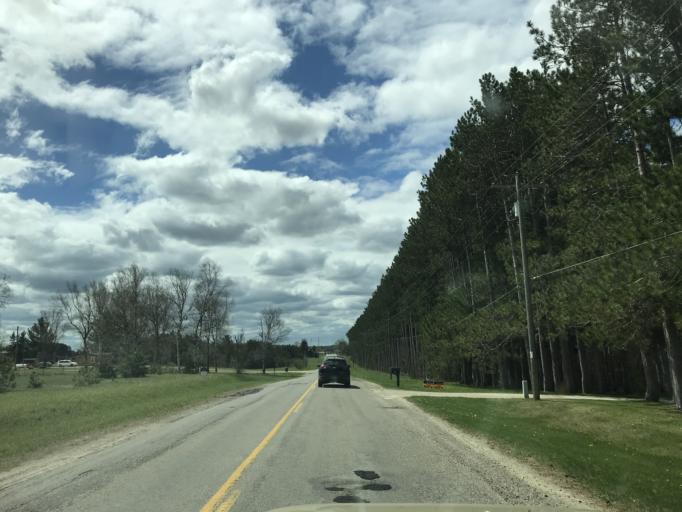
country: US
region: Michigan
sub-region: Otsego County
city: Gaylord
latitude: 45.0390
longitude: -84.6942
